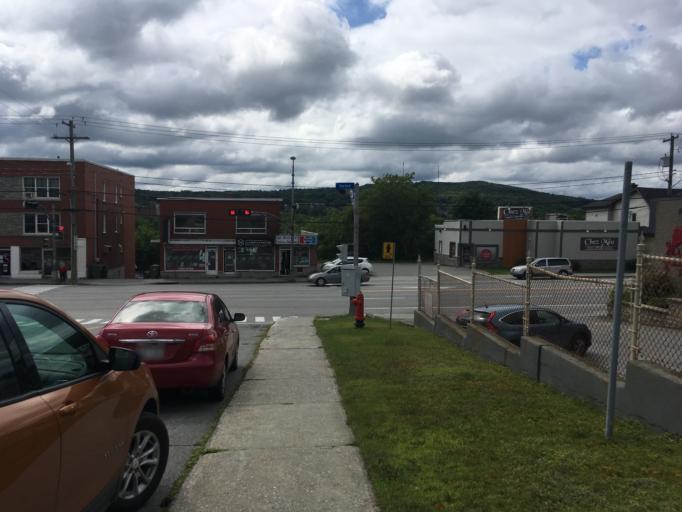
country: CA
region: Quebec
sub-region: Estrie
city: Sherbrooke
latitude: 45.3991
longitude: -71.9080
